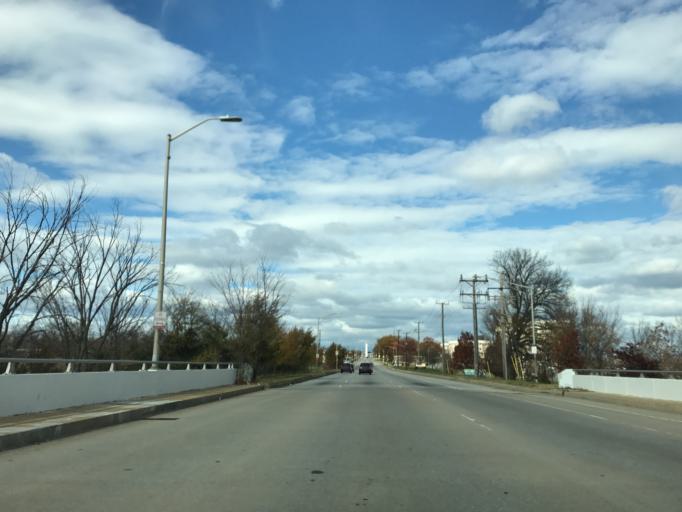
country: US
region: Maryland
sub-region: Anne Arundel County
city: Brooklyn Park
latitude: 39.2476
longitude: -76.6119
